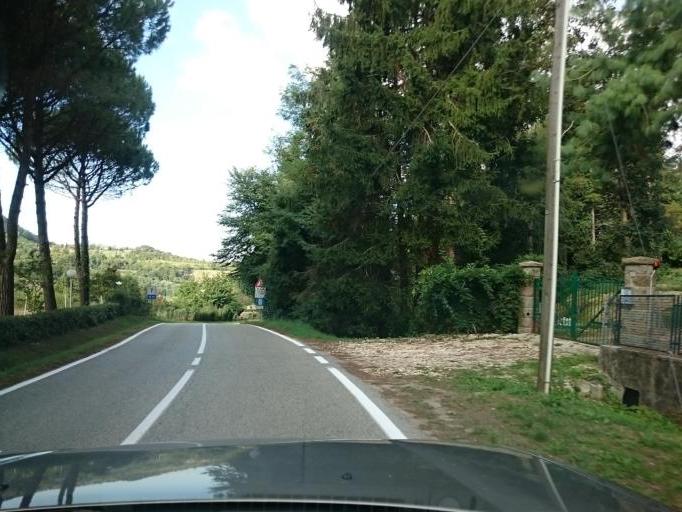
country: IT
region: Veneto
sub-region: Provincia di Padova
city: Galzignano
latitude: 45.3247
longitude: 11.7060
